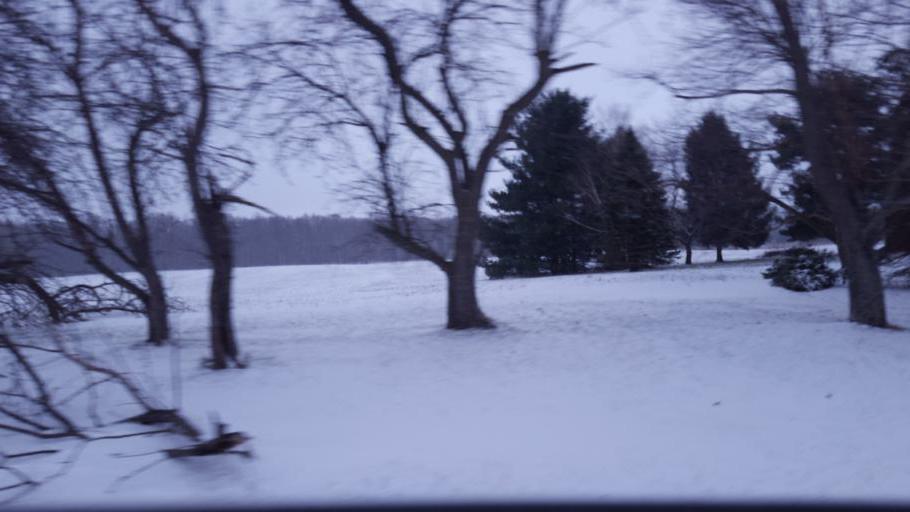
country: US
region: Ohio
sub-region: Morrow County
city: Mount Gilead
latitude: 40.5201
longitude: -82.7928
